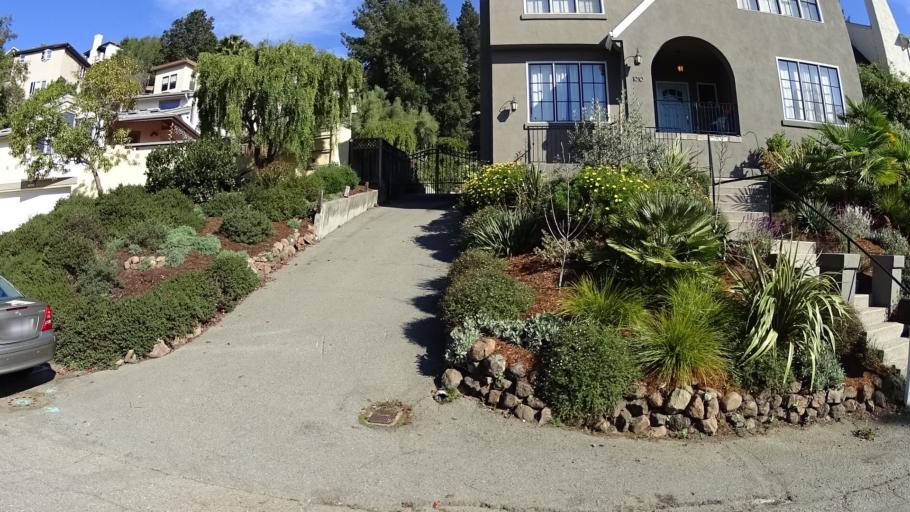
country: US
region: California
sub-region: Alameda County
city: Piedmont
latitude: 37.8408
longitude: -122.2199
